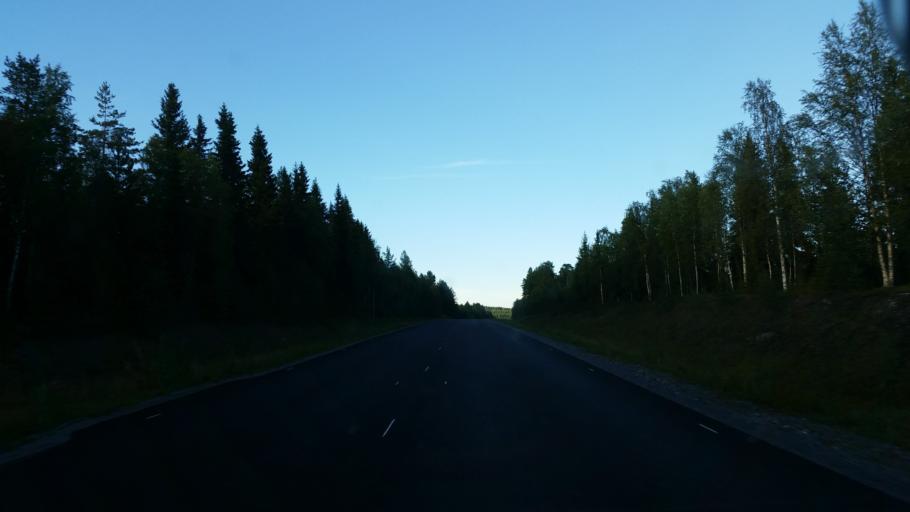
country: SE
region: Vaesterbotten
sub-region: Dorotea Kommun
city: Dorotea
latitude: 64.2926
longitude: 16.5332
